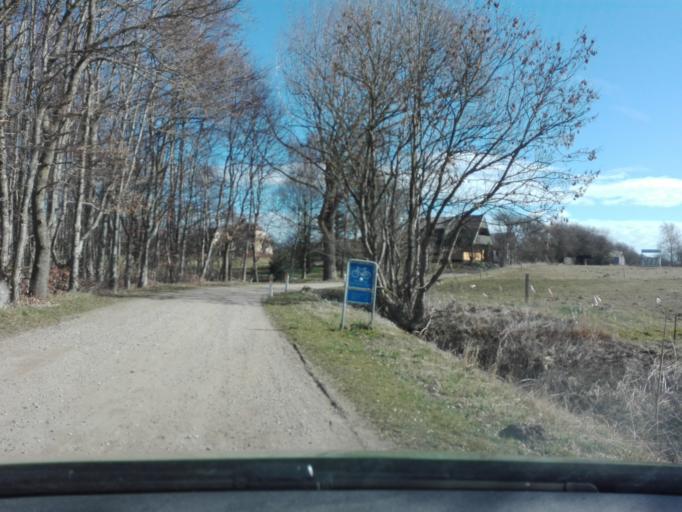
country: DK
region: Central Jutland
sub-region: Horsens Kommune
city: Horsens
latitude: 55.8874
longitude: 9.9612
